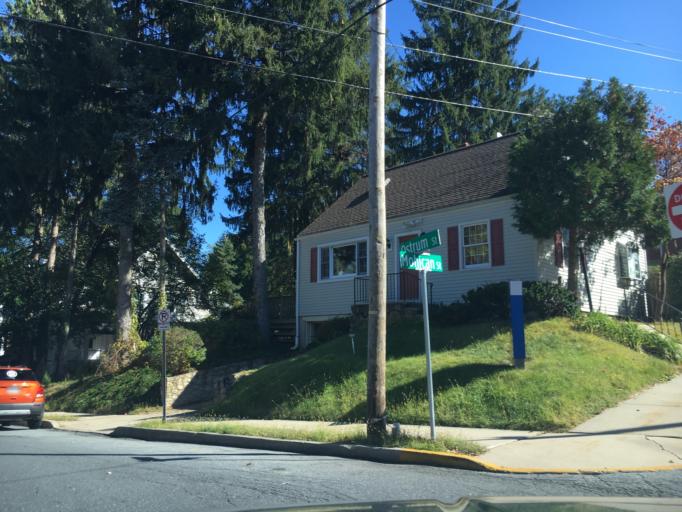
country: US
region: Pennsylvania
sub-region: Lehigh County
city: Fountain Hill
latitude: 40.6098
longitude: -75.3915
